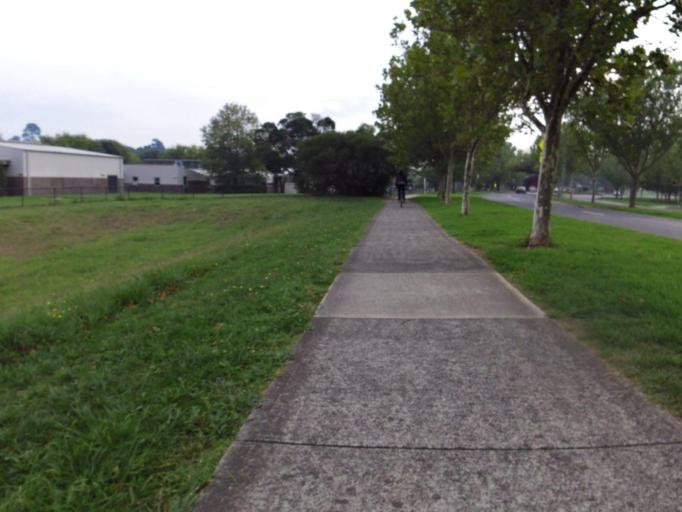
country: AU
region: Victoria
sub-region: Casey
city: Narre Warren
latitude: -38.0167
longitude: 145.3228
